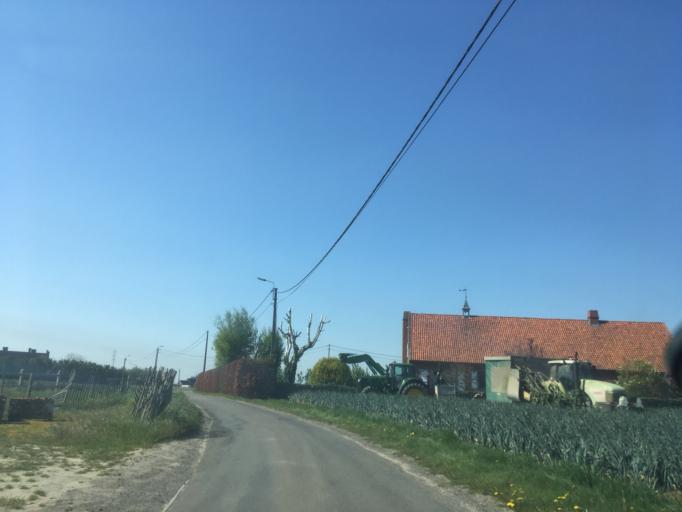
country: BE
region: Flanders
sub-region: Provincie West-Vlaanderen
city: Ardooie
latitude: 50.9603
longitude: 3.2184
